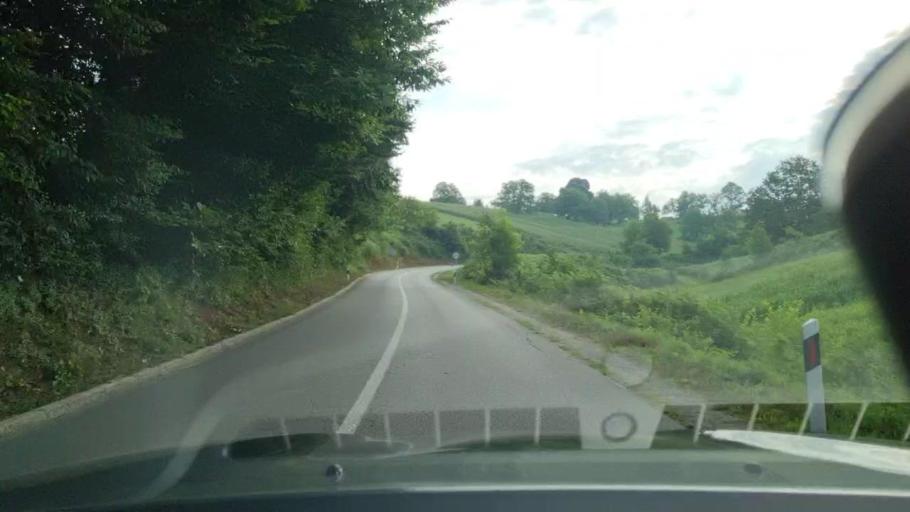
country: BA
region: Federation of Bosnia and Herzegovina
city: Podzvizd
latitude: 45.1741
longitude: 15.8677
